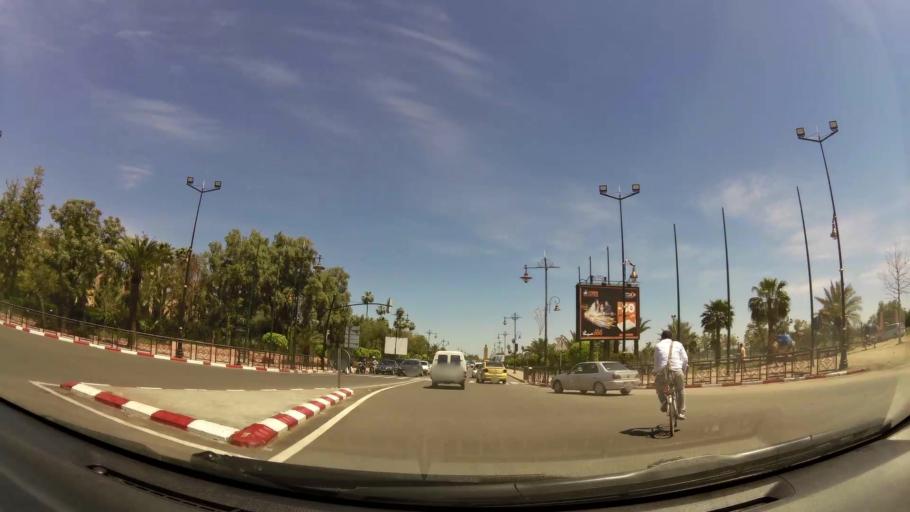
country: MA
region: Marrakech-Tensift-Al Haouz
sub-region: Marrakech
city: Marrakesh
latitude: 31.6179
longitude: -8.0078
